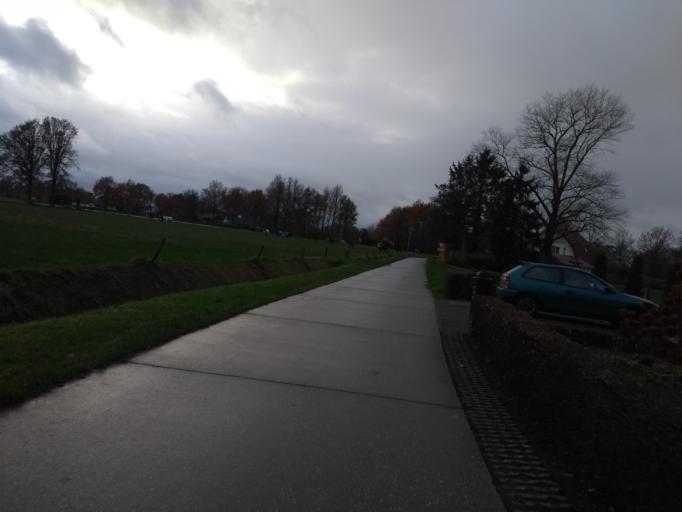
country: NL
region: Overijssel
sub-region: Gemeente Tubbergen
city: Tubbergen
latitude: 52.3910
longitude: 6.7251
